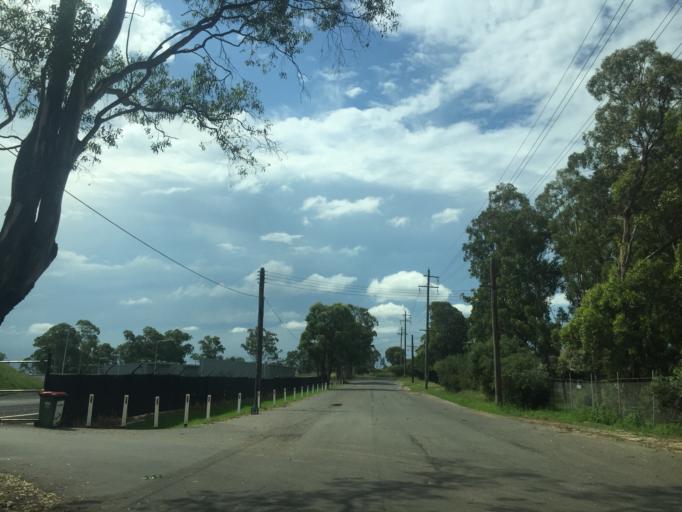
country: AU
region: New South Wales
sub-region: Holroyd
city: Girraween
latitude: -33.8079
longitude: 150.9138
